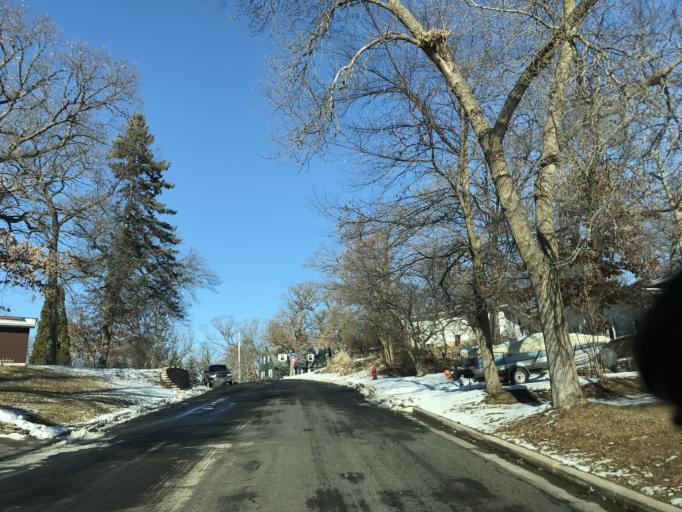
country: US
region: Wisconsin
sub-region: Dane County
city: Monona
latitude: 43.0503
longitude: -89.3278
